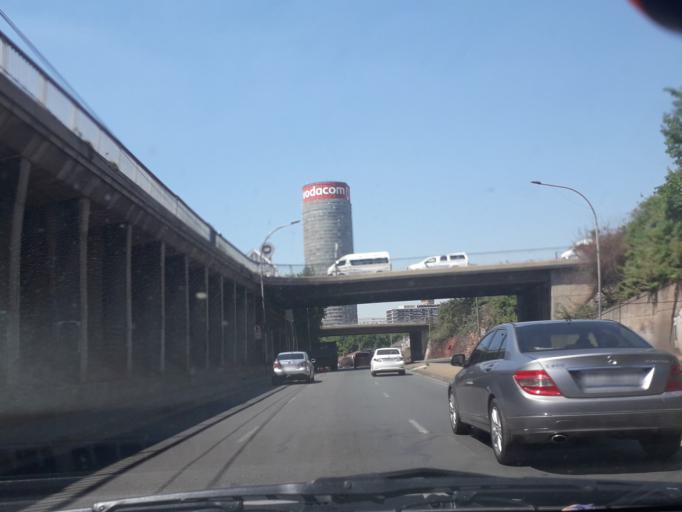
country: ZA
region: Gauteng
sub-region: City of Johannesburg Metropolitan Municipality
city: Johannesburg
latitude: -26.1848
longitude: 28.0578
